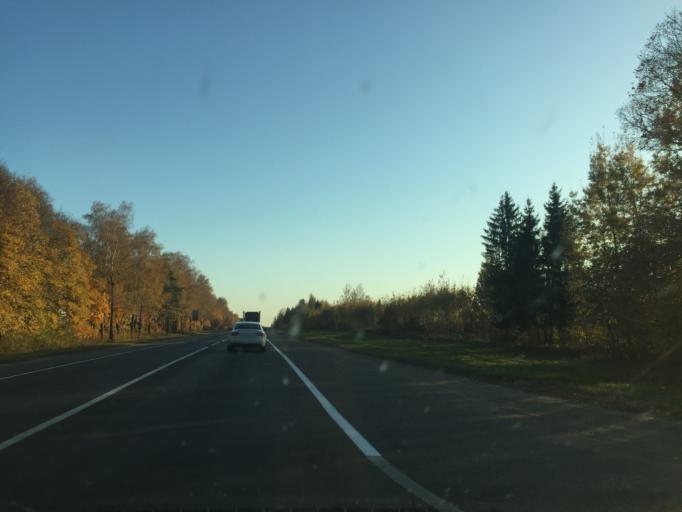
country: BY
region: Mogilev
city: Poselok Voskhod
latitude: 53.7531
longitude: 30.3653
